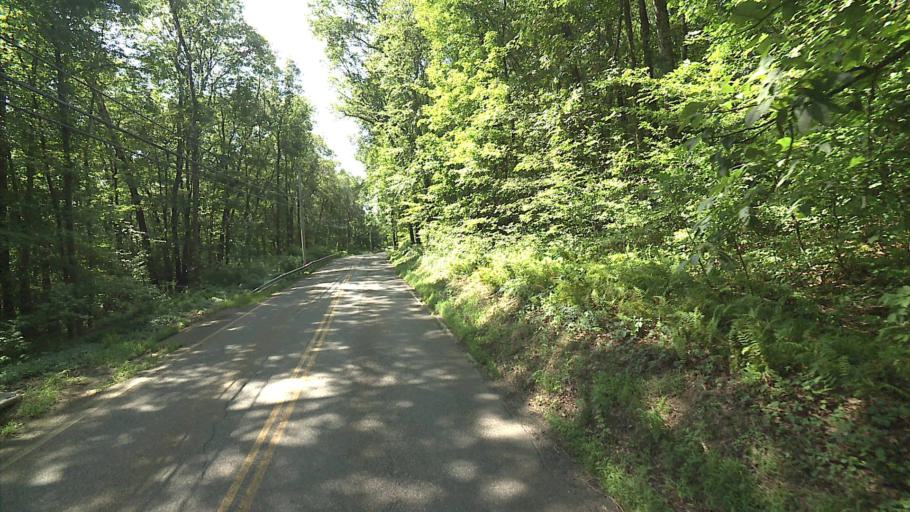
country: US
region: Connecticut
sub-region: Tolland County
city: Stafford
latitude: 41.9526
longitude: -72.1909
